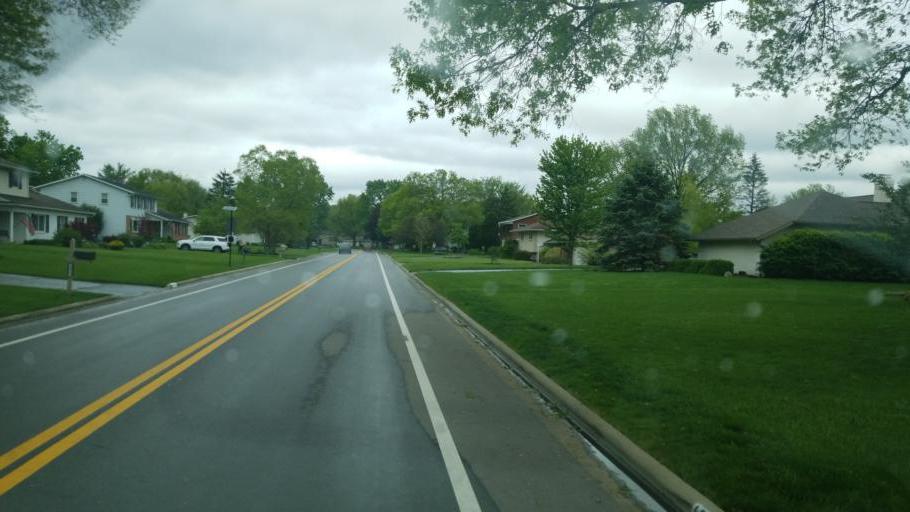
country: US
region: Ohio
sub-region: Delaware County
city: Powell
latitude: 40.1239
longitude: -83.0497
